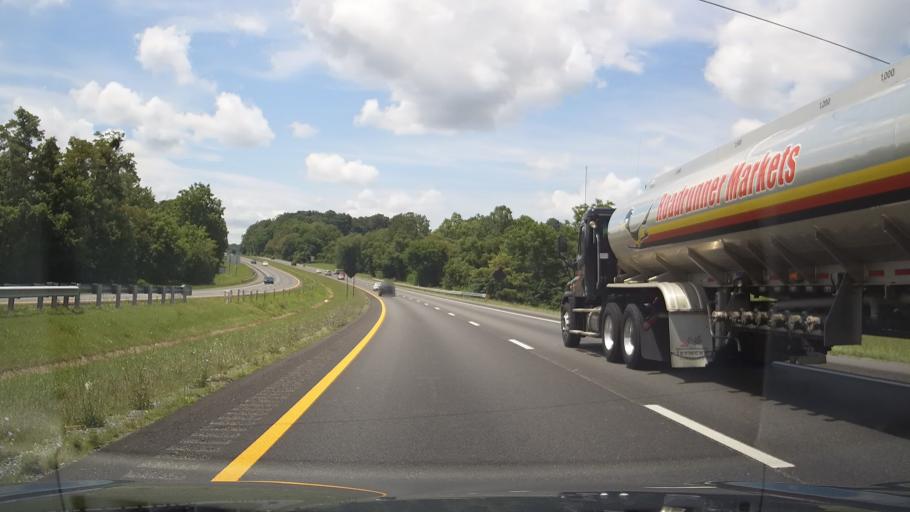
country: US
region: Tennessee
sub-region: Washington County
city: Oak Grove
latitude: 36.3680
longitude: -82.4139
